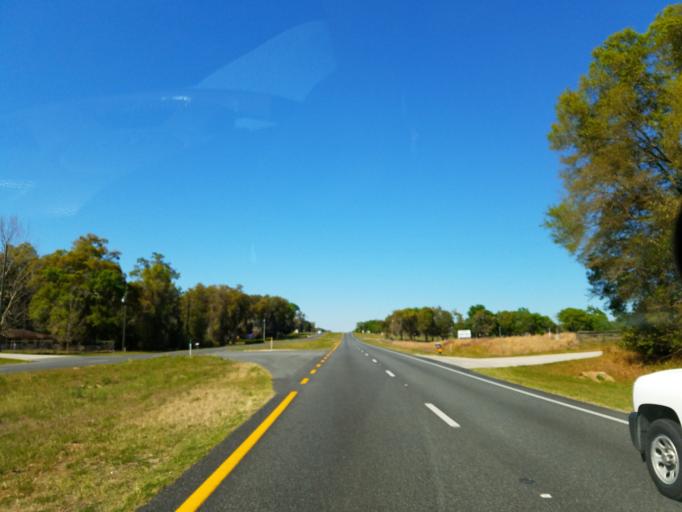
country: US
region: Florida
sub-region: Marion County
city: Belleview
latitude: 29.0377
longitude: -82.0448
